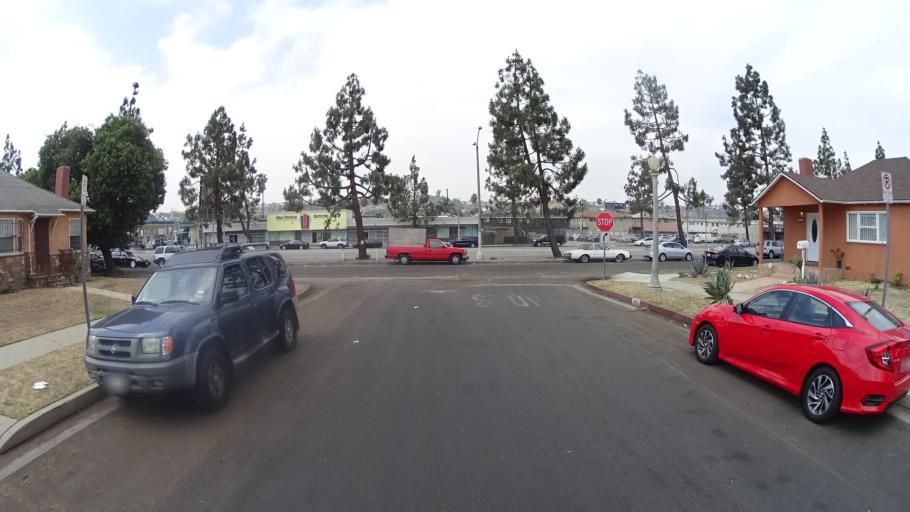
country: US
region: California
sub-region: Los Angeles County
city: View Park-Windsor Hills
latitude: 34.0156
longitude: -118.3423
